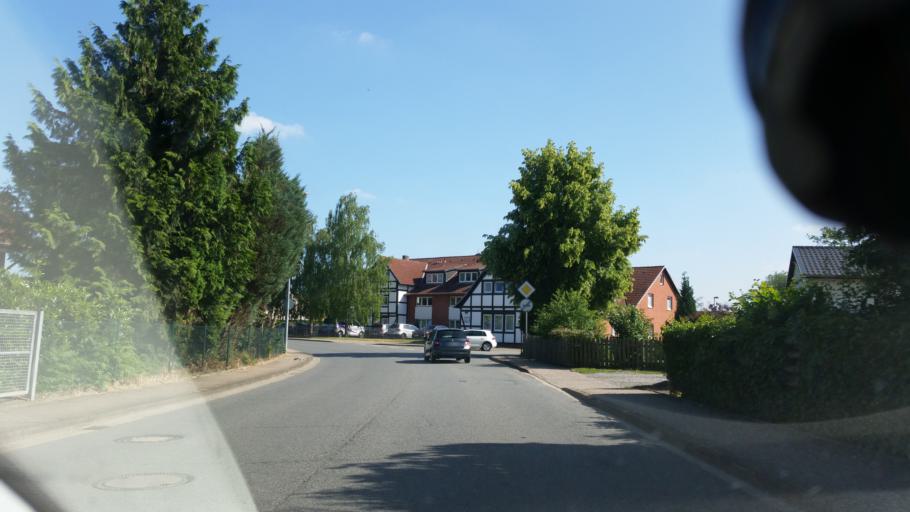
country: DE
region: Lower Saxony
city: Wolfsburg
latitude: 52.3485
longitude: 10.7791
